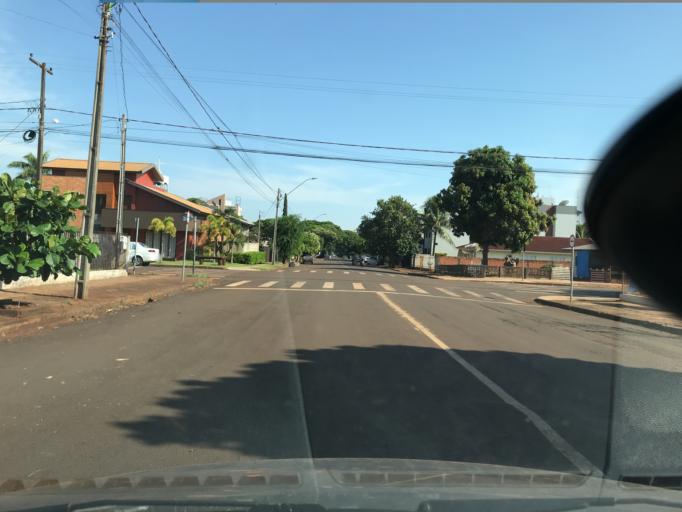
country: BR
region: Parana
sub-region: Palotina
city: Palotina
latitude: -24.2883
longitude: -53.8409
